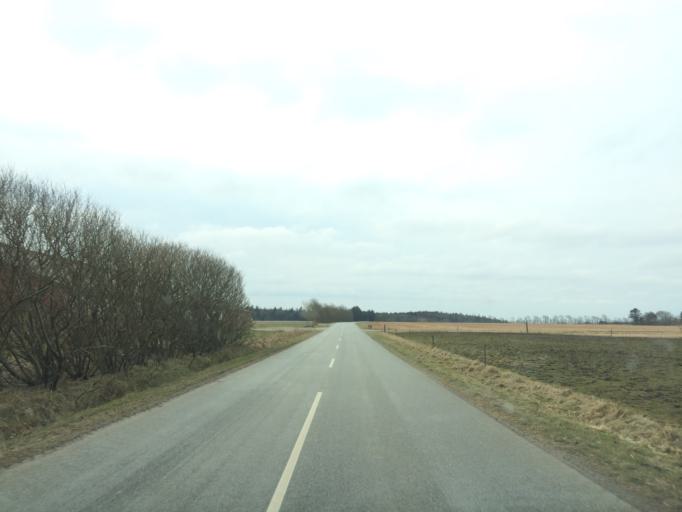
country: DK
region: Central Jutland
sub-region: Ringkobing-Skjern Kommune
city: Tarm
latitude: 55.8082
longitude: 8.3892
